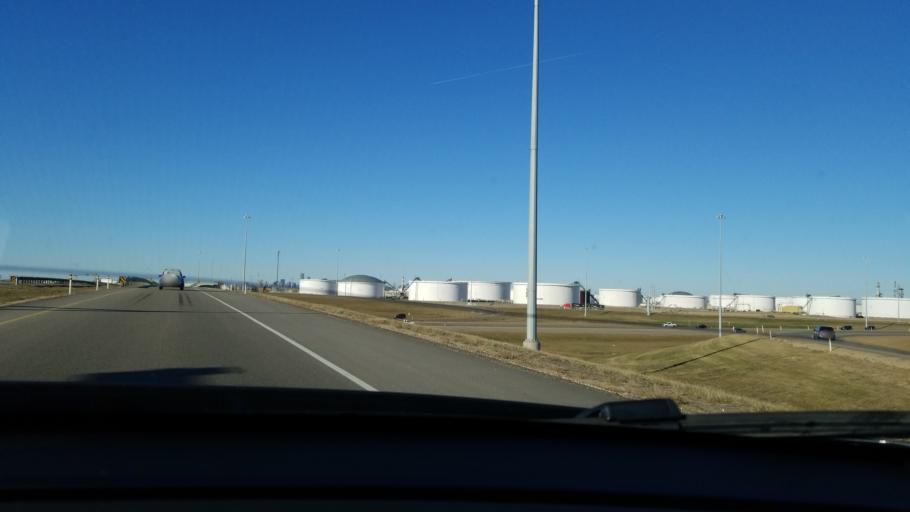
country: CA
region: Alberta
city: Sherwood Park
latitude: 53.5409
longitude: -113.3392
